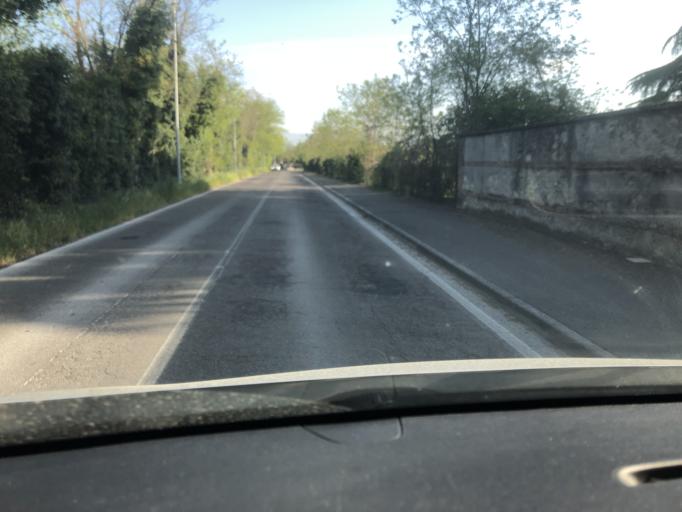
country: IT
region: Veneto
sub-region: Provincia di Verona
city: Verona
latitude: 45.4153
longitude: 10.9993
